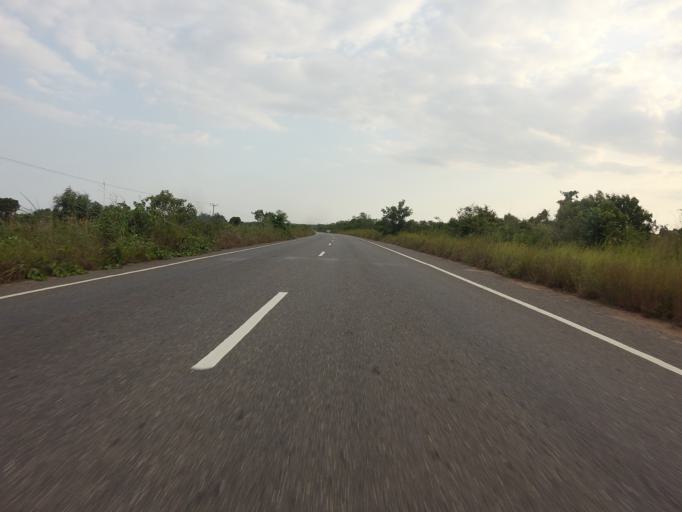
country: GH
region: Volta
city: Ho
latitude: 6.1332
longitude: 0.5246
